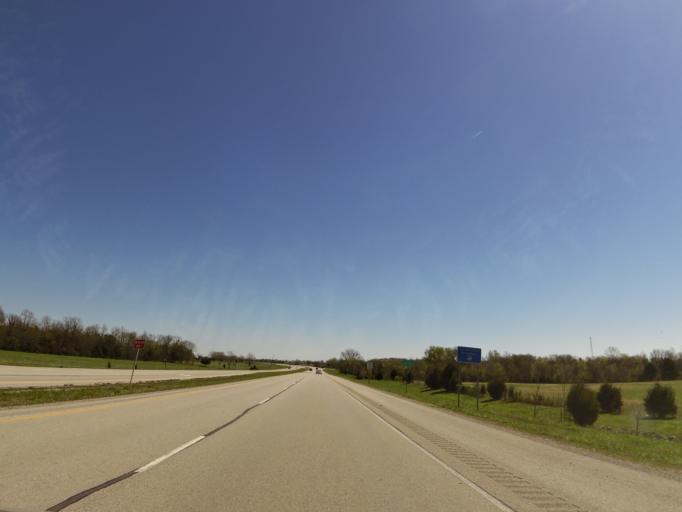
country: US
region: Kentucky
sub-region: Logan County
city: Auburn
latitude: 36.8920
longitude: -86.6169
